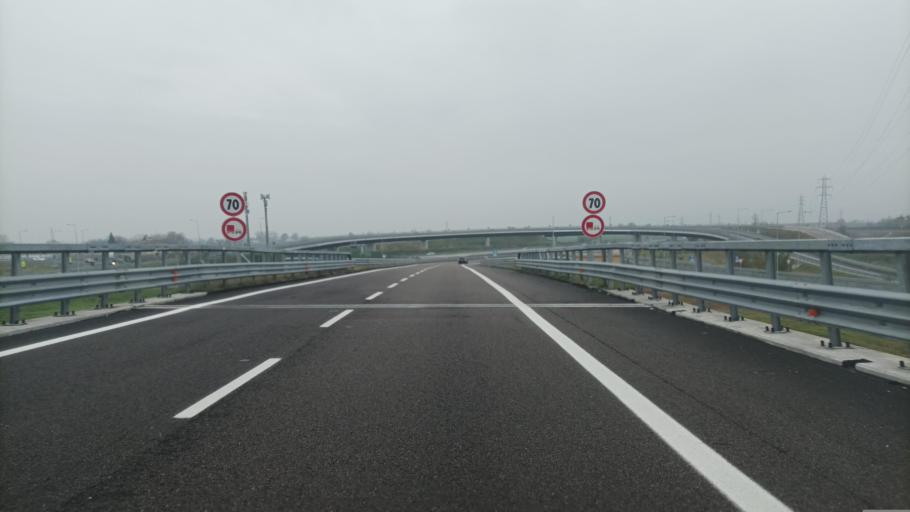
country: IT
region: Emilia-Romagna
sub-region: Provincia di Parma
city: Ponte Taro
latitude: 44.8668
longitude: 10.2332
